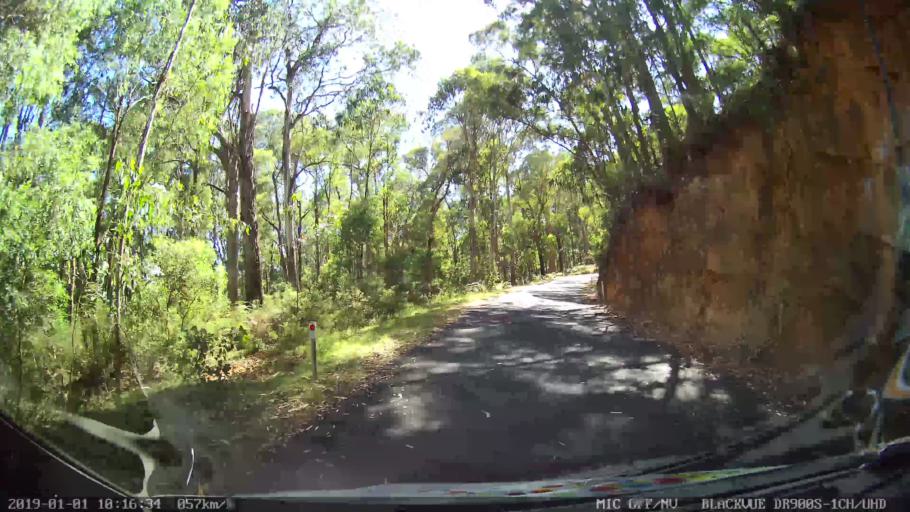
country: AU
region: New South Wales
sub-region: Snowy River
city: Jindabyne
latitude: -36.0933
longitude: 148.1683
